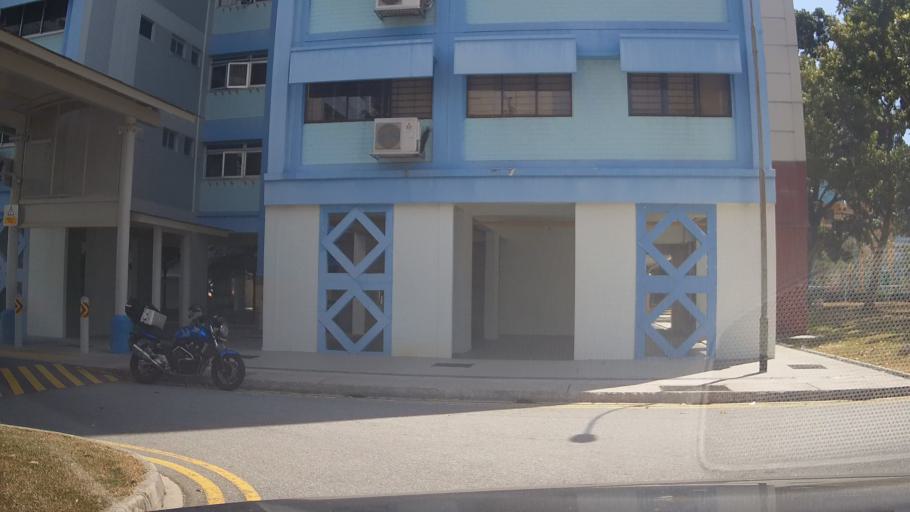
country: MY
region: Johor
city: Kampung Pasir Gudang Baru
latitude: 1.3733
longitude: 103.9554
